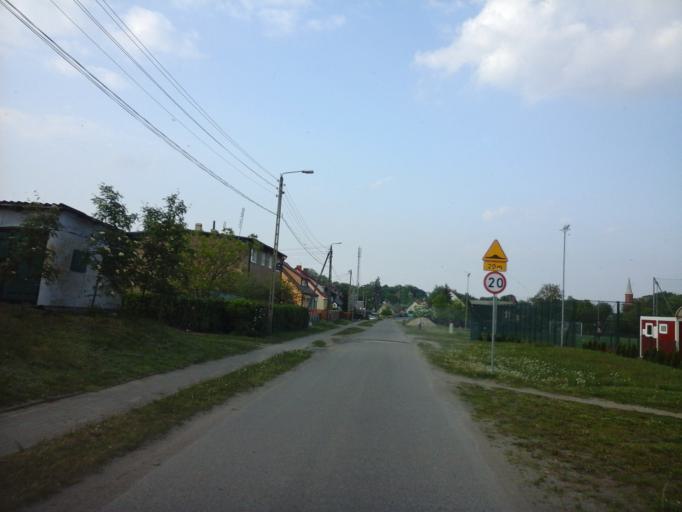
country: PL
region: West Pomeranian Voivodeship
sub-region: Powiat choszczenski
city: Krzecin
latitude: 53.0016
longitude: 15.4168
